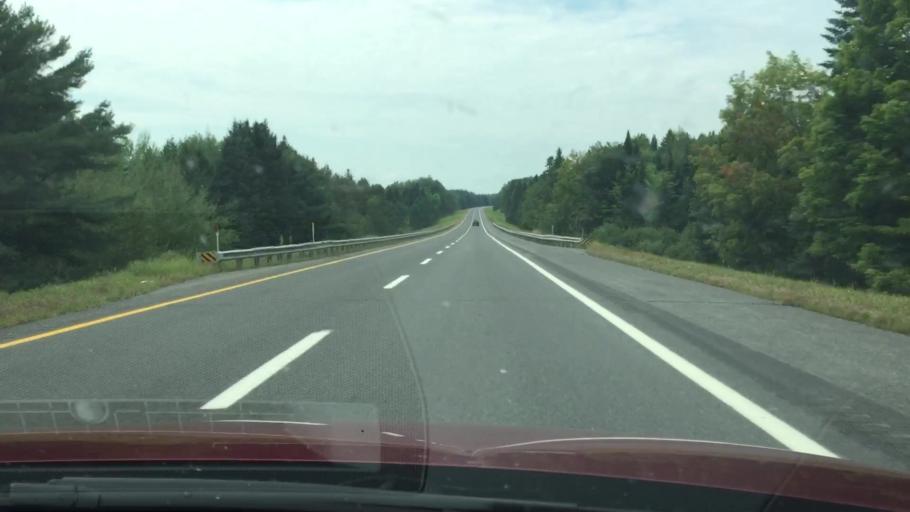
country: US
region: Maine
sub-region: Aroostook County
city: Houlton
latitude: 46.1372
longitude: -67.8931
